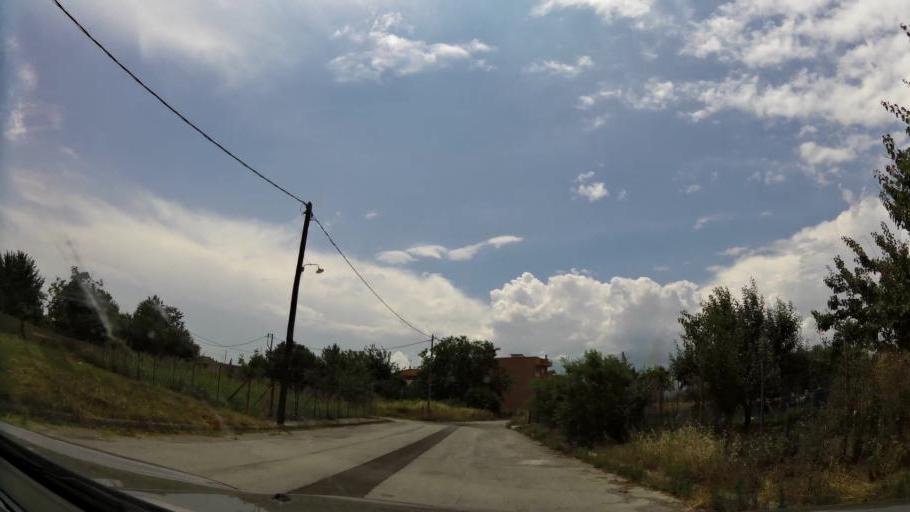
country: GR
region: Central Macedonia
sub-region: Nomos Pierias
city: Peristasi
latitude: 40.2628
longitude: 22.5345
